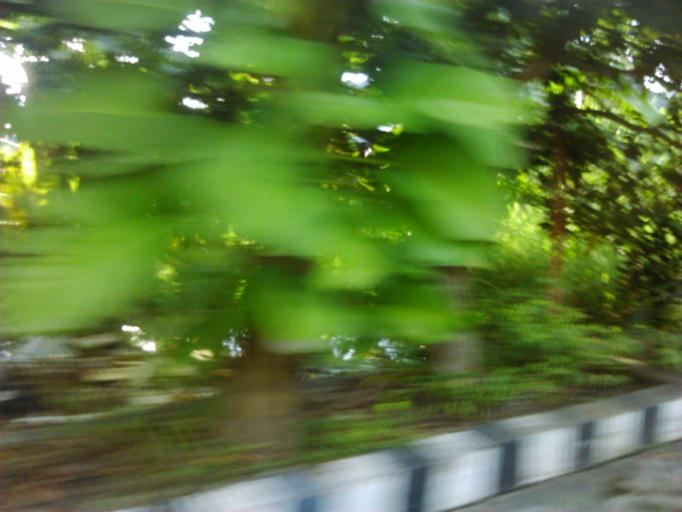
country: ID
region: East Java
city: Wonorejo
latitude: -7.2903
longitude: 112.8035
